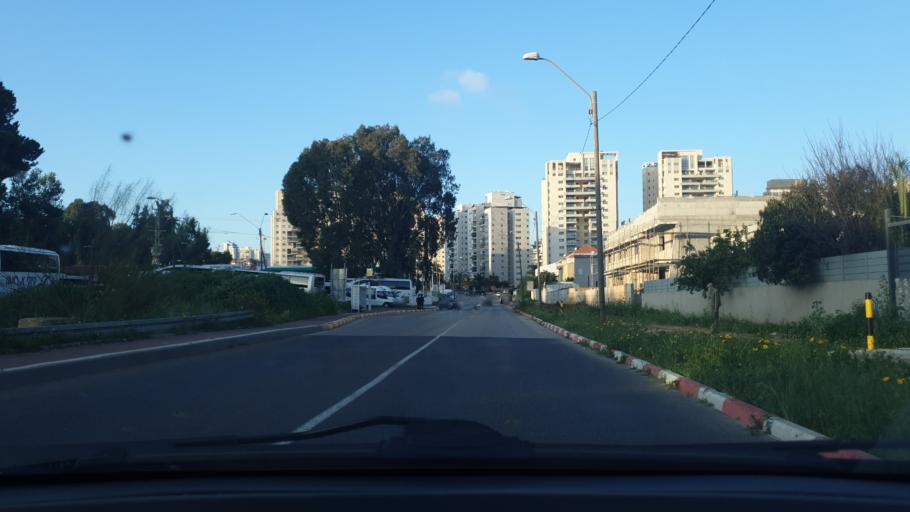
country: IL
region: Central District
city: Ness Ziona
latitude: 31.9350
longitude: 34.8314
